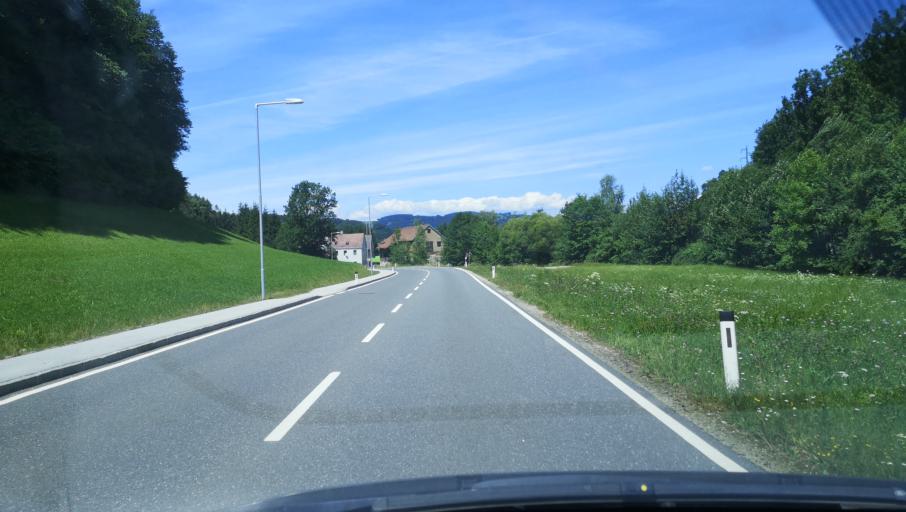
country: AT
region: Lower Austria
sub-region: Politischer Bezirk Scheibbs
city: Gresten
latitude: 47.9638
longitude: 15.0238
